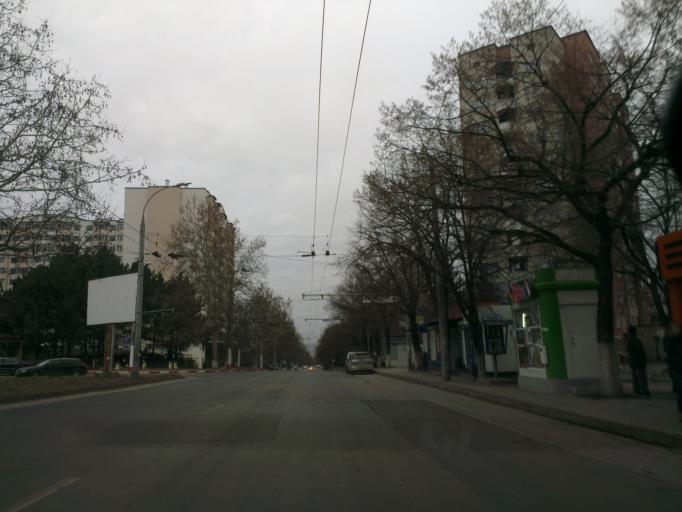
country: MD
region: Chisinau
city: Chisinau
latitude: 46.9867
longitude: 28.8447
